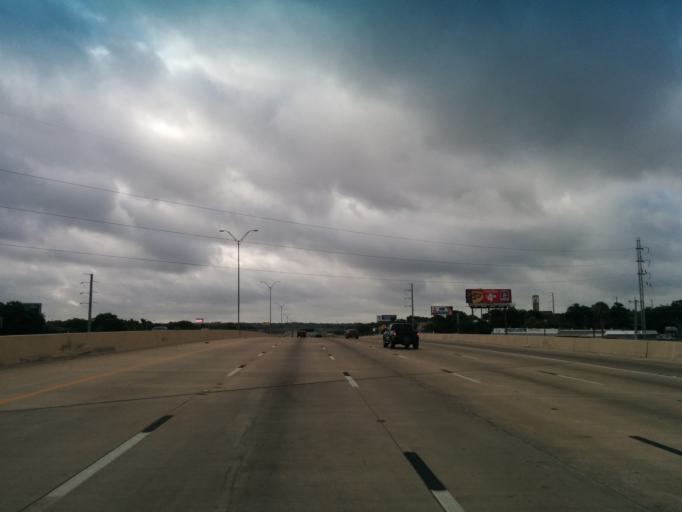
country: US
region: Texas
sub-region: Bexar County
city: Balcones Heights
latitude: 29.4818
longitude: -98.5267
